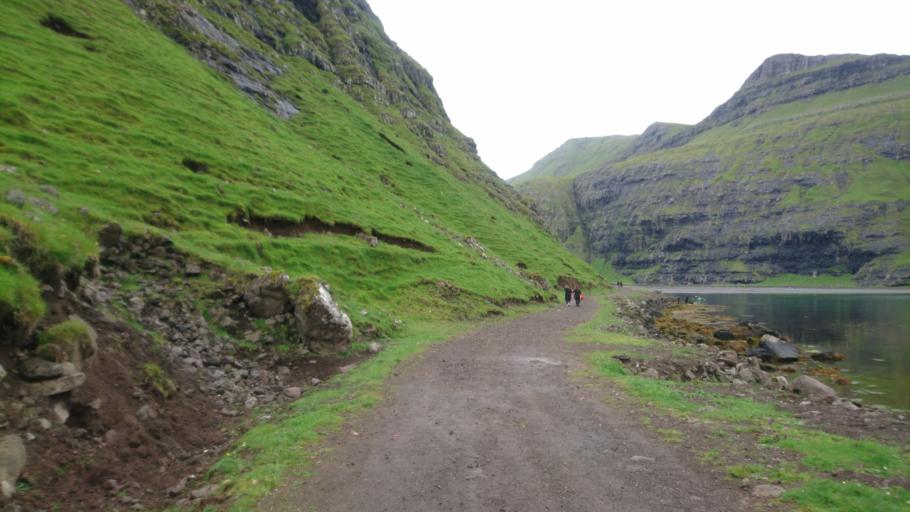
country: FO
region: Streymoy
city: Vestmanna
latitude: 62.2458
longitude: -7.1876
